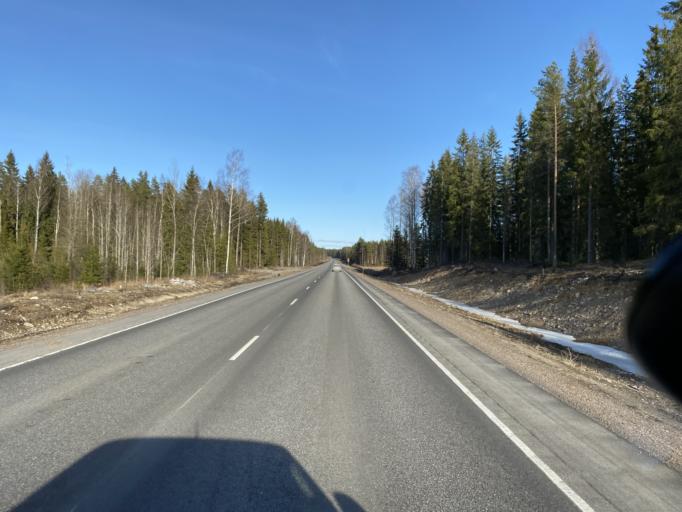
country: FI
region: Satakunta
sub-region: Pori
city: Huittinen
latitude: 61.1739
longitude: 22.5422
